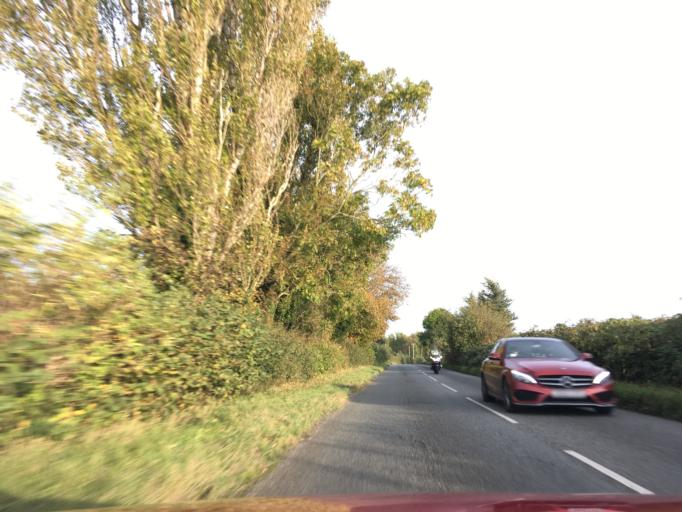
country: GB
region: England
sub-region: South Gloucestershire
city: Almondsbury
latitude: 51.5916
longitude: -2.5882
